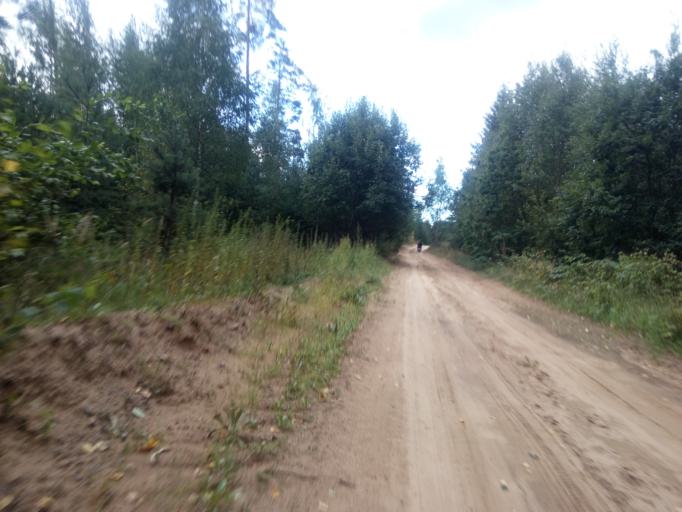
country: BY
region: Vitebsk
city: Dzisna
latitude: 55.6923
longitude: 28.3573
